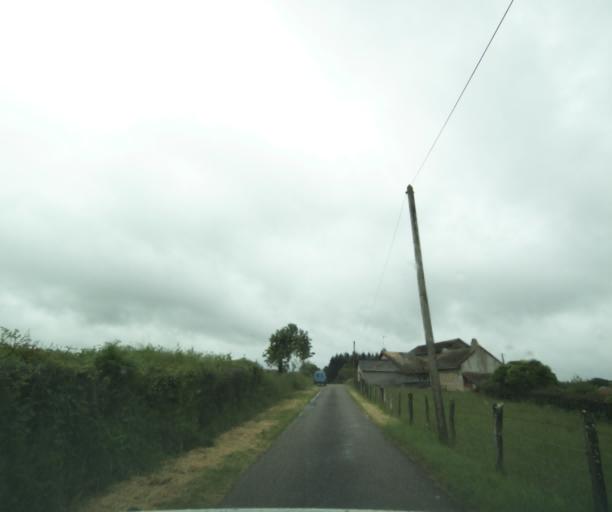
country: FR
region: Bourgogne
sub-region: Departement de Saone-et-Loire
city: Charolles
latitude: 46.4815
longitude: 4.4148
